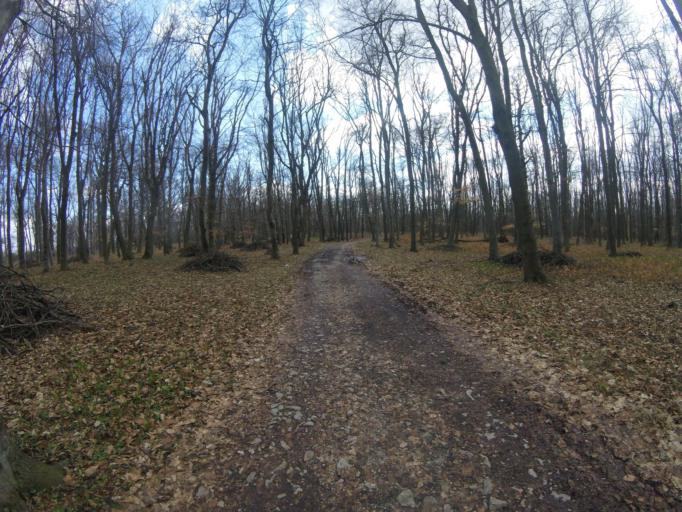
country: HU
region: Komarom-Esztergom
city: Tardos
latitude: 47.6790
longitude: 18.4883
